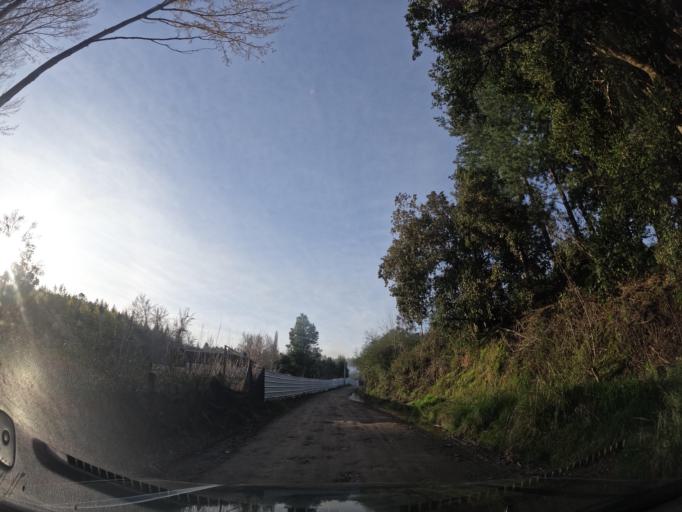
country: CL
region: Biobio
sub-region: Provincia de Concepcion
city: Concepcion
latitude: -36.8649
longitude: -72.9988
